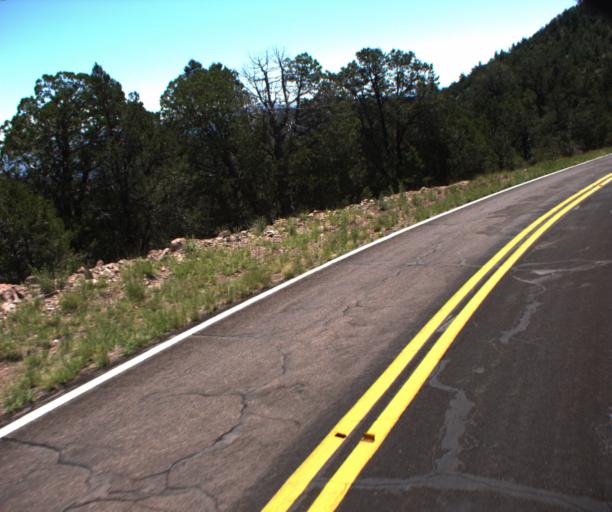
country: US
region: Arizona
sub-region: Greenlee County
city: Morenci
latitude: 33.3981
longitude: -109.3358
